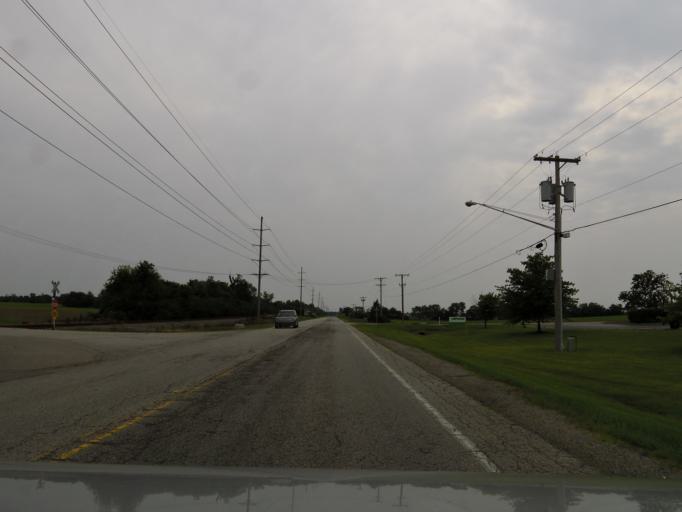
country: US
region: Ohio
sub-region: Clinton County
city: Wilmington
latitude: 39.4127
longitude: -83.8455
